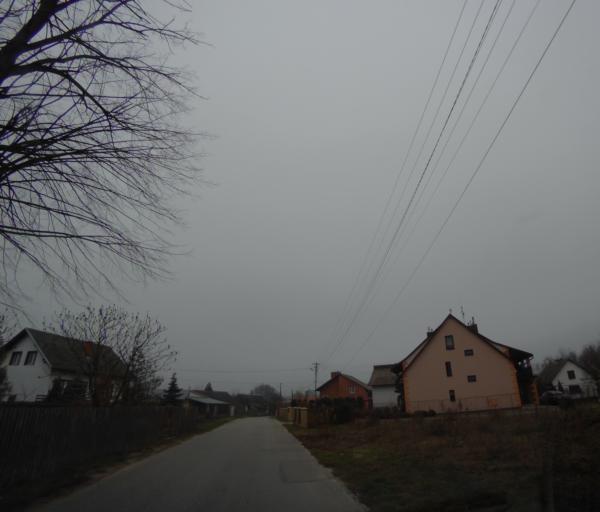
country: PL
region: Subcarpathian Voivodeship
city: Nowa Sarzyna
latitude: 50.2957
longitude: 22.3530
